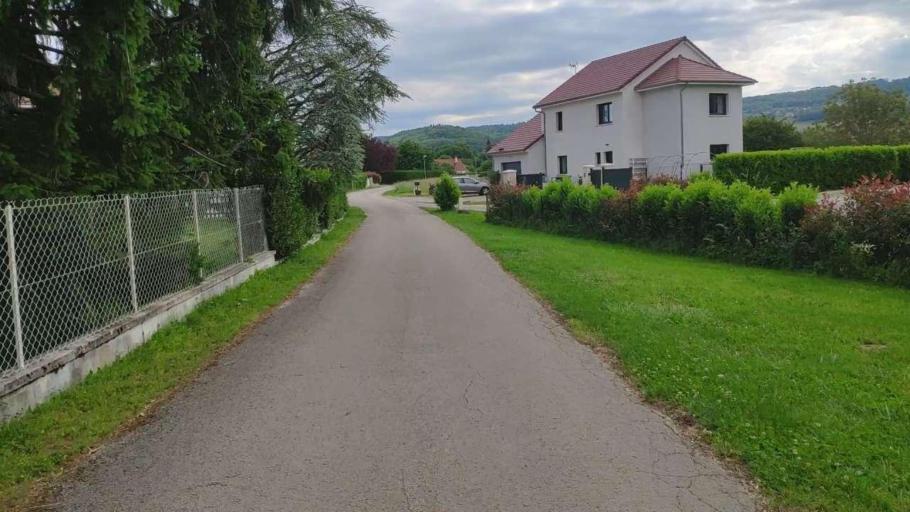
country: FR
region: Franche-Comte
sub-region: Departement du Jura
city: Perrigny
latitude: 46.7613
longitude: 5.5903
